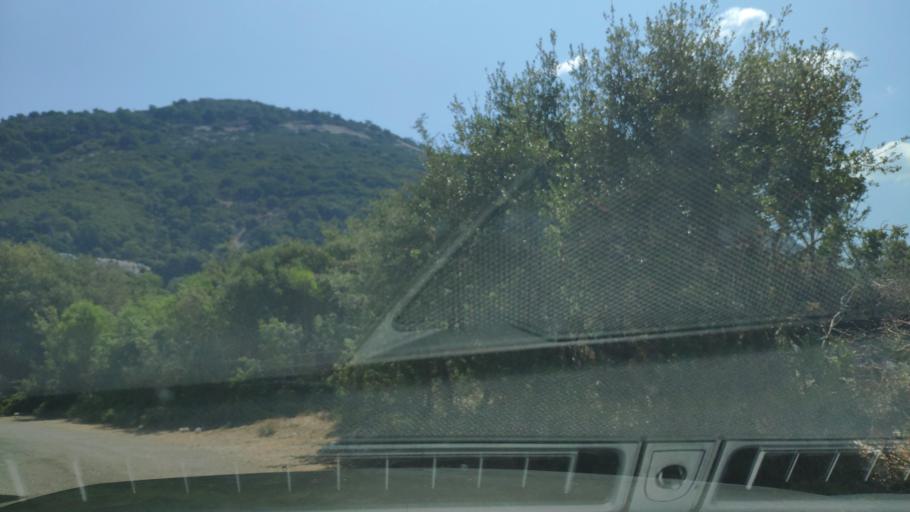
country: GR
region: West Greece
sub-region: Nomos Aitolias kai Akarnanias
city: Monastirakion
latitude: 38.8205
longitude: 20.9308
